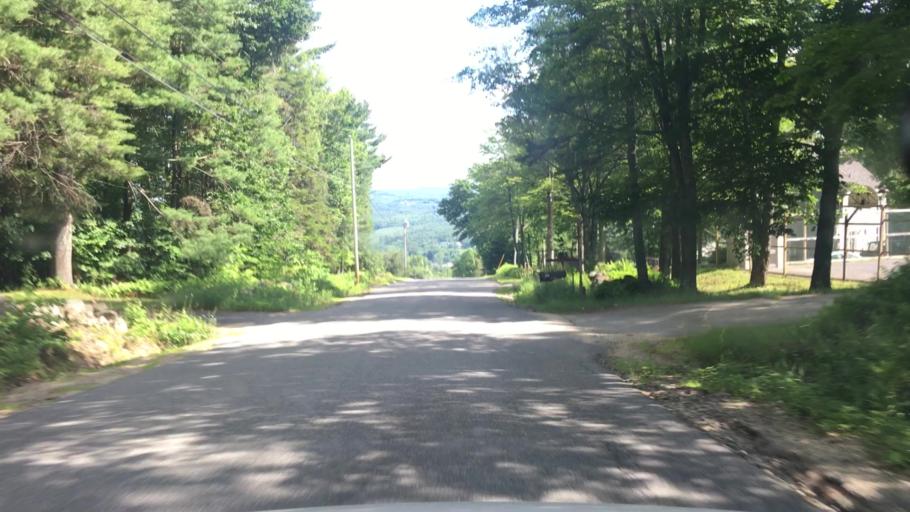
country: US
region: Maine
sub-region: Franklin County
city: Wilton
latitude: 44.6344
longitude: -70.1982
